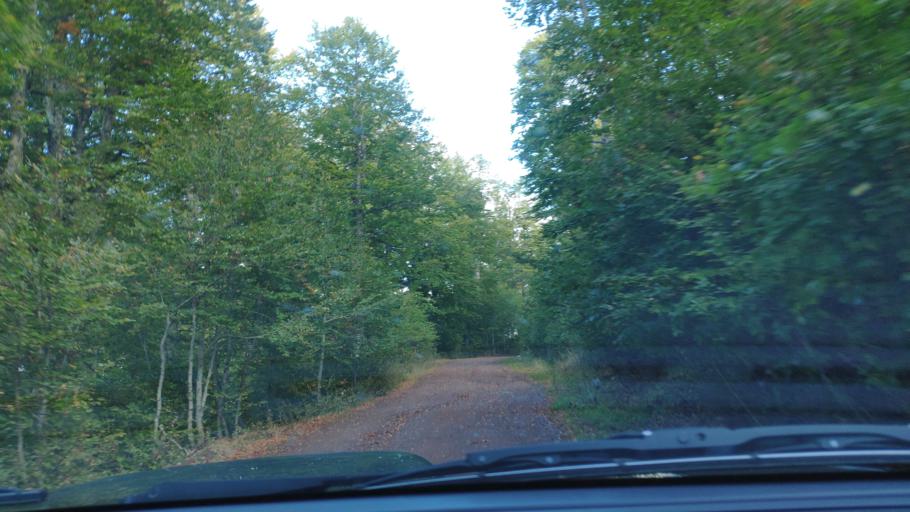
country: GR
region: West Macedonia
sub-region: Nomos Kastorias
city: Nestorio
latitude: 40.3146
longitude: 20.9113
